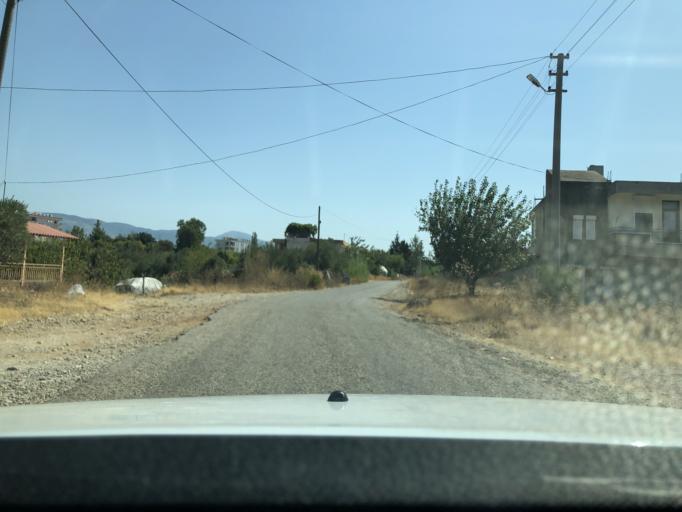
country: TR
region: Antalya
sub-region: Manavgat
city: Manavgat
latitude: 36.8042
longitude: 31.4726
